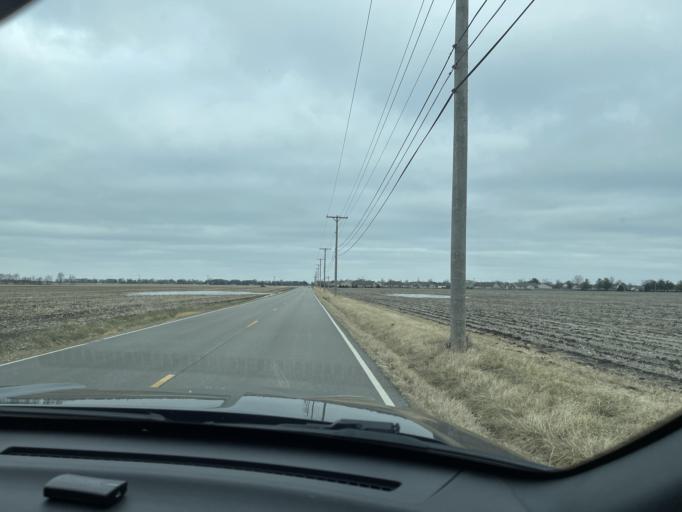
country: US
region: Illinois
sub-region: Sangamon County
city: Jerome
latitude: 39.7664
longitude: -89.7534
